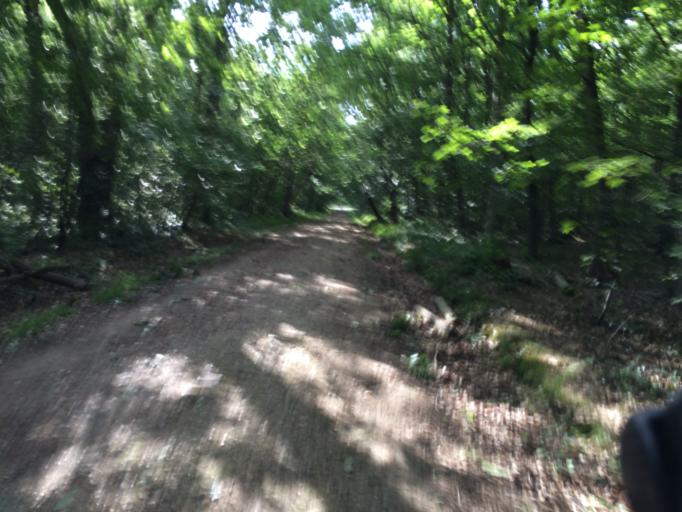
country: FR
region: Ile-de-France
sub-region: Departement de l'Essonne
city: Igny
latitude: 48.7511
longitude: 2.2435
